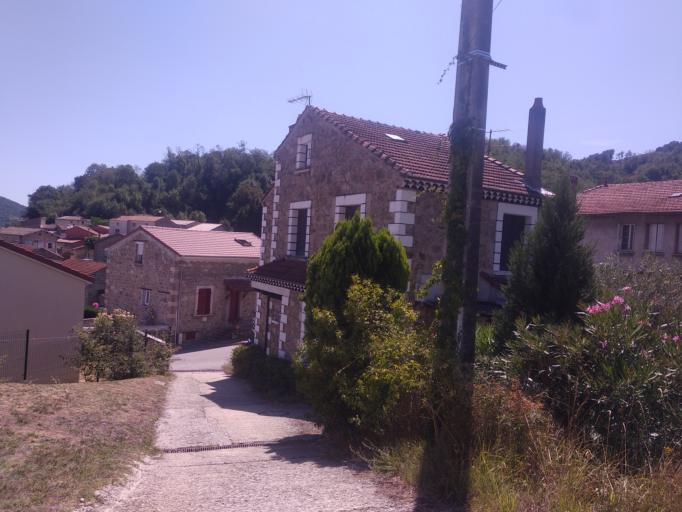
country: FR
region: Rhone-Alpes
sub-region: Departement de l'Ardeche
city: Sarras
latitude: 45.1868
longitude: 4.7950
